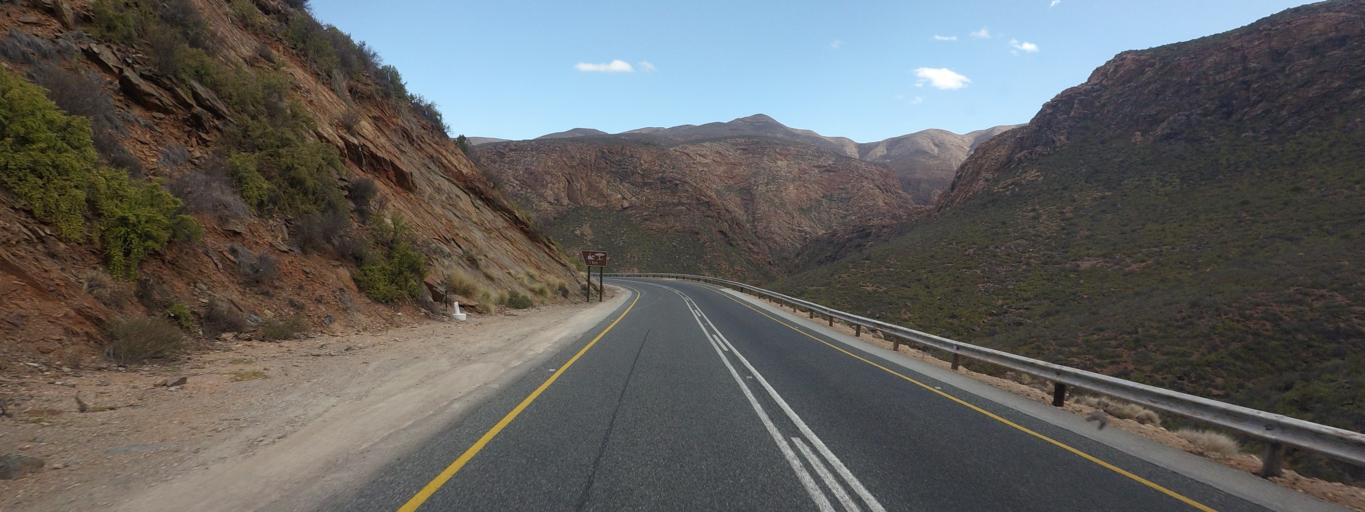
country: ZA
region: Western Cape
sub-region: Eden District Municipality
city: Ladismith
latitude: -33.4970
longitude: 21.5829
